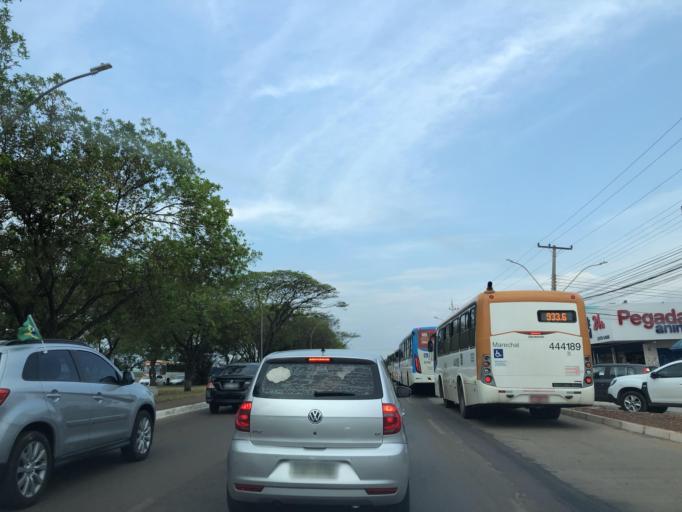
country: BR
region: Federal District
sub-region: Brasilia
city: Brasilia
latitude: -15.8186
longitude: -48.1057
